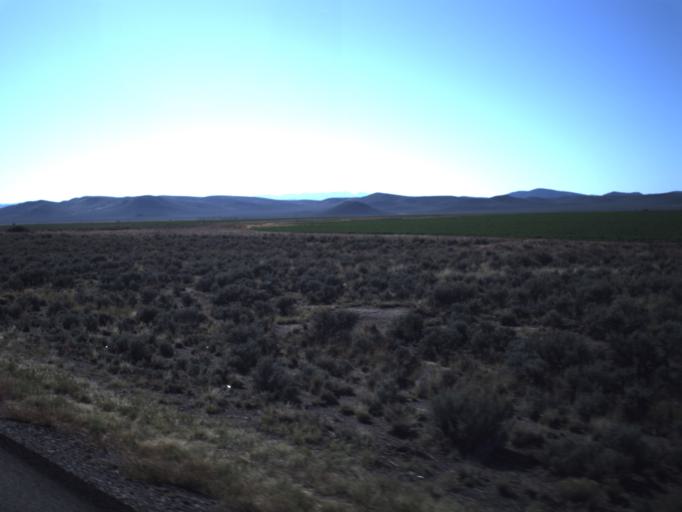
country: US
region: Utah
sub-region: Washington County
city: Enterprise
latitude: 37.7622
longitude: -113.8053
